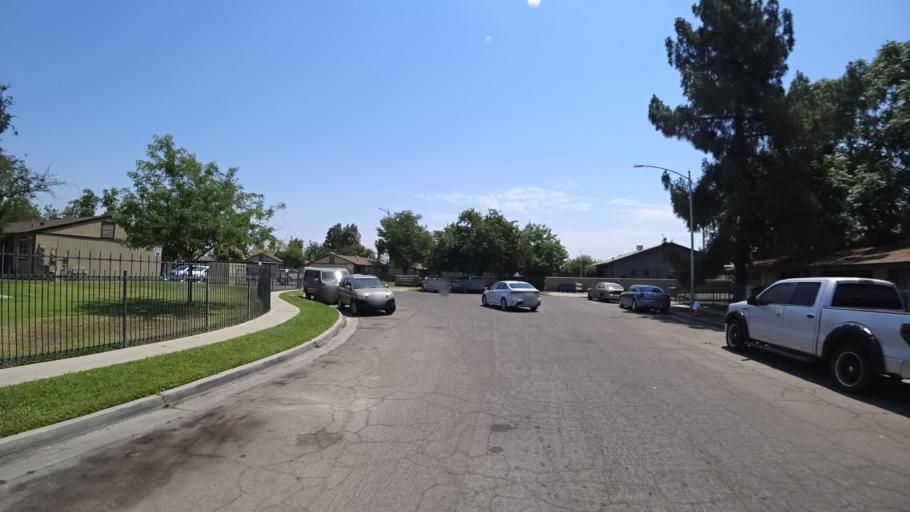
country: US
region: California
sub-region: Fresno County
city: Fresno
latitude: 36.7196
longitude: -119.8010
